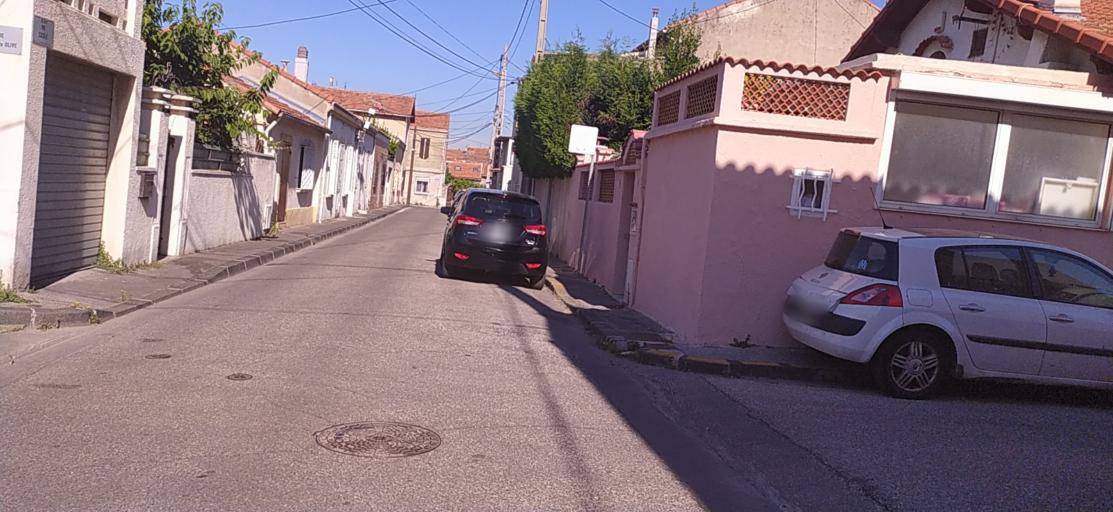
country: FR
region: Provence-Alpes-Cote d'Azur
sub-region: Departement des Bouches-du-Rhone
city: Marseille 16
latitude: 43.3545
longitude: 5.3441
